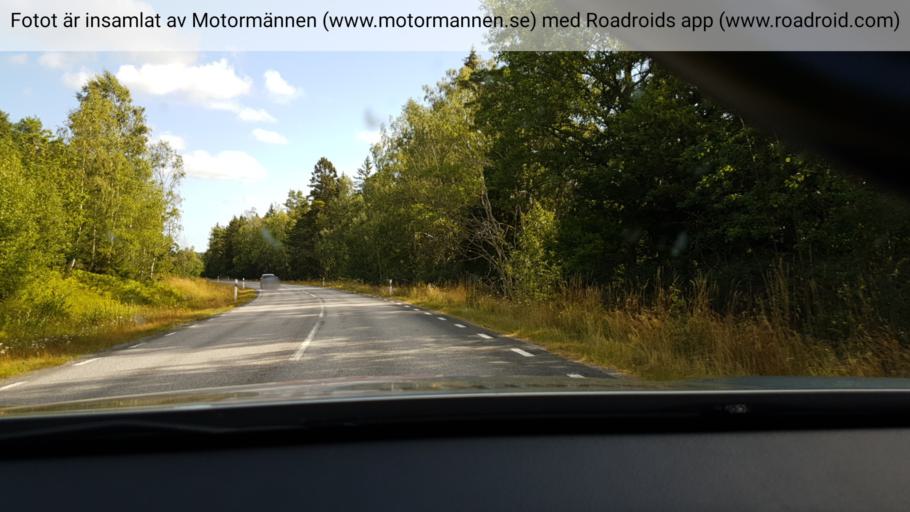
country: SE
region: Stockholm
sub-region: Norrtalje Kommun
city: Norrtalje
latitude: 59.5825
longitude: 18.6587
